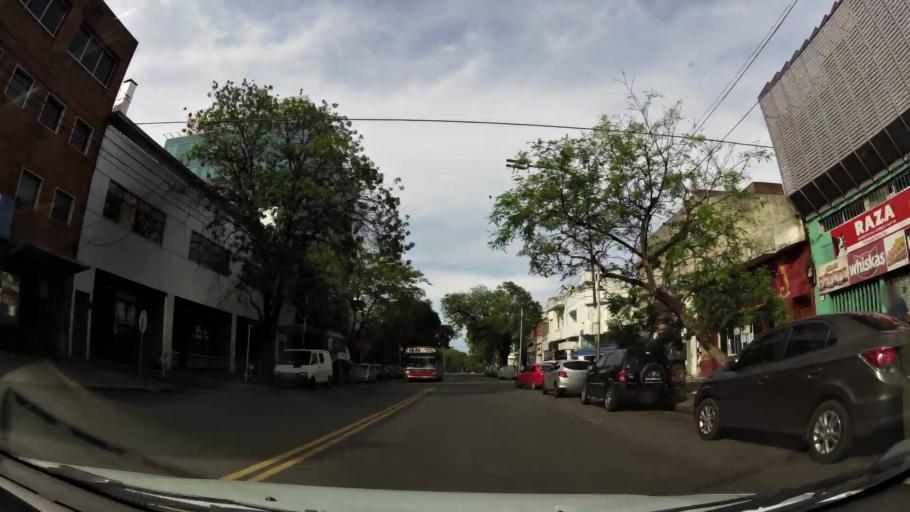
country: AR
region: Buenos Aires F.D.
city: Villa Lugano
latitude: -34.6492
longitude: -58.4890
